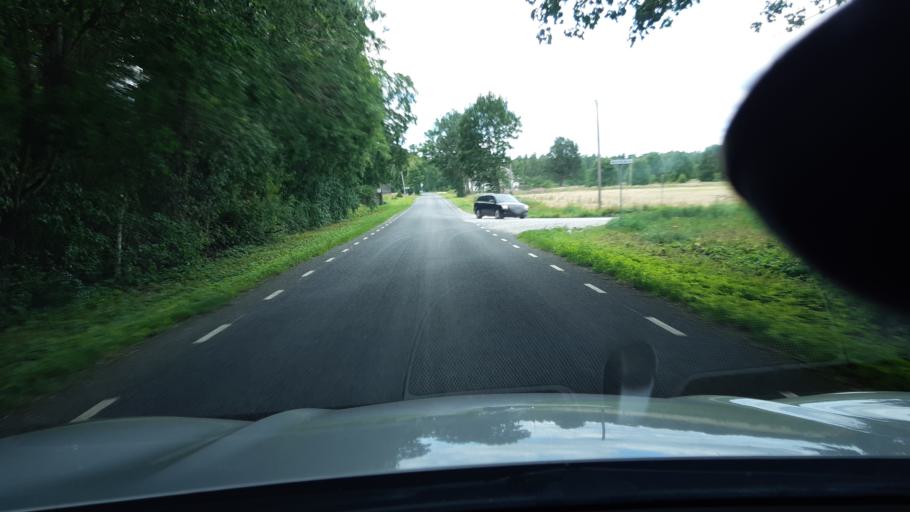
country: EE
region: Raplamaa
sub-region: Jaervakandi vald
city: Jarvakandi
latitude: 58.8766
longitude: 24.7493
